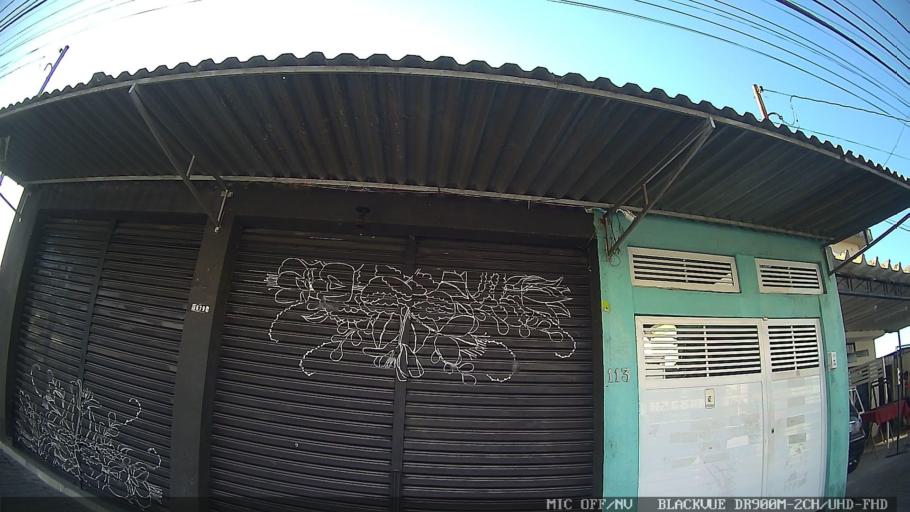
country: BR
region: Sao Paulo
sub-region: Santos
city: Santos
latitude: -23.9625
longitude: -46.2951
